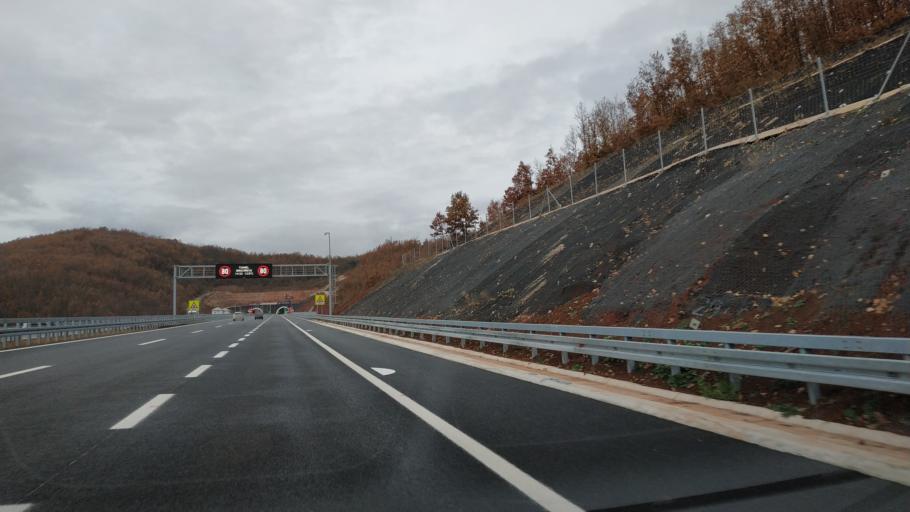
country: RS
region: Central Serbia
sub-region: Nisavski Okrug
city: Gadzin Han
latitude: 43.2634
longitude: 22.1440
